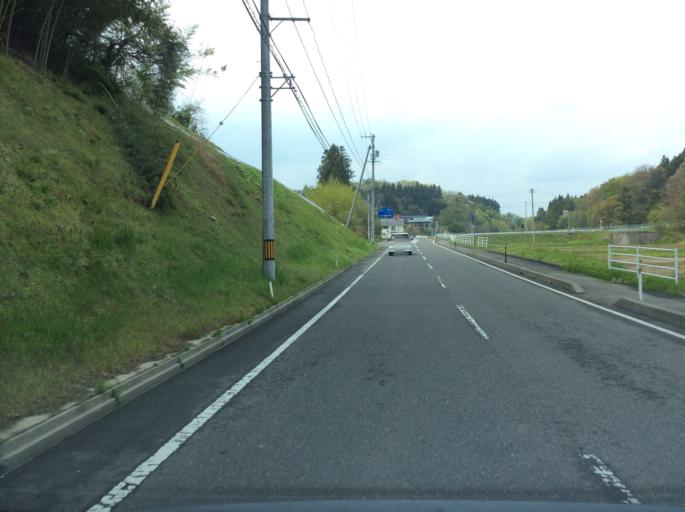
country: JP
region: Fukushima
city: Miharu
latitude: 37.3968
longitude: 140.4900
